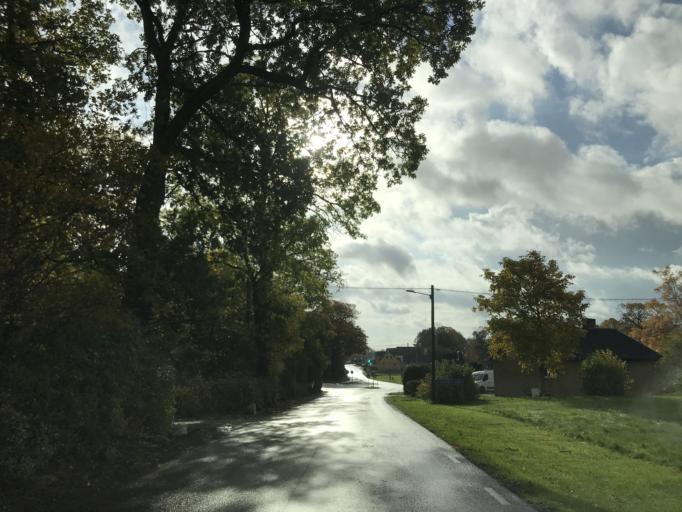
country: SE
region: Skane
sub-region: Svalovs Kommun
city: Teckomatorp
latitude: 55.8723
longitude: 13.1176
